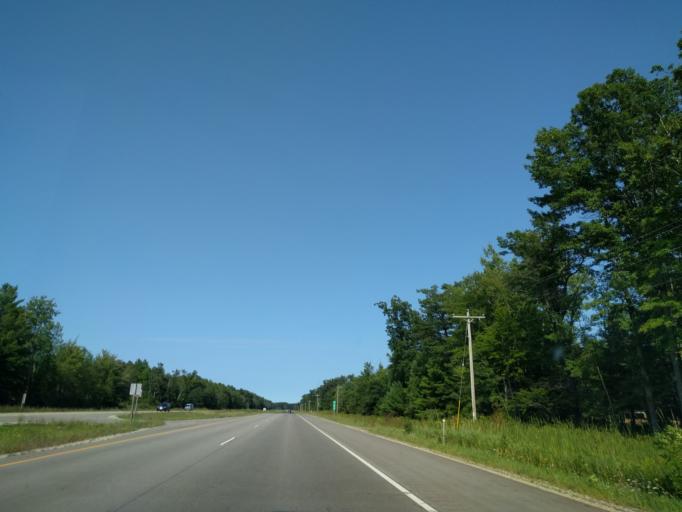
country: US
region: Wisconsin
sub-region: Oconto County
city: Oconto
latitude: 44.8417
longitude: -87.9112
